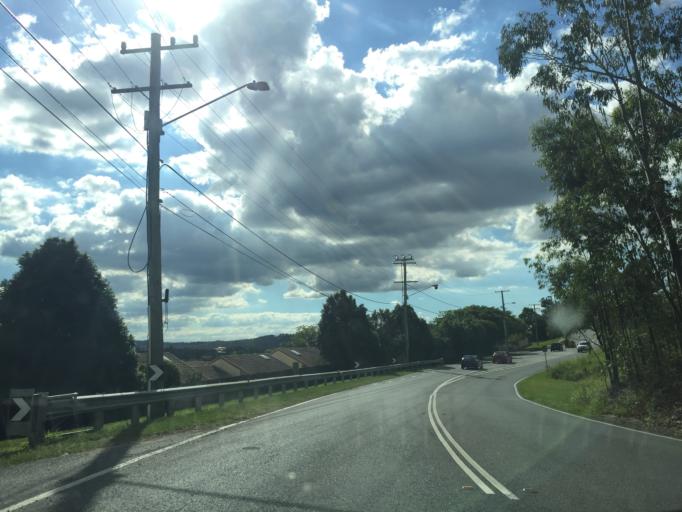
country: AU
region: Queensland
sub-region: Moreton Bay
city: Ferny Hills
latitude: -27.4219
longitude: 152.9478
